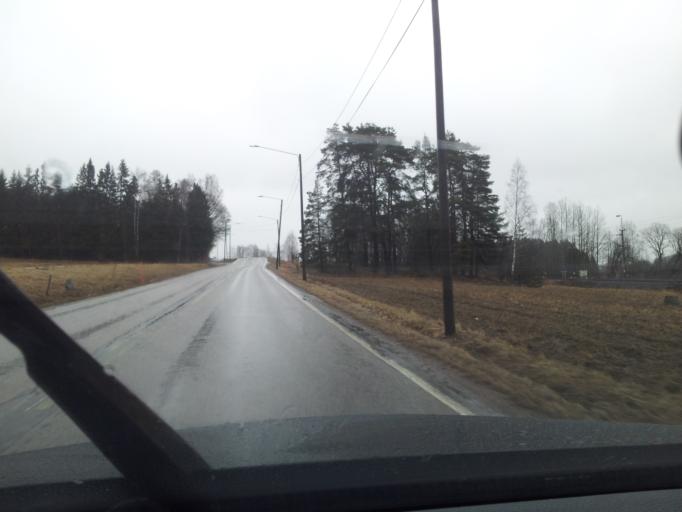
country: FI
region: Uusimaa
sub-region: Helsinki
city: Kirkkonummi
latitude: 60.1452
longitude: 24.5228
